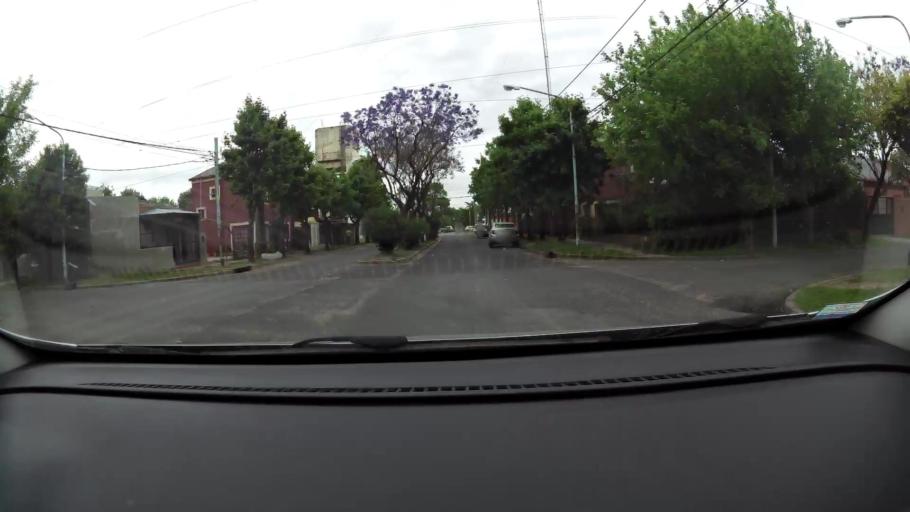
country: AR
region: Buenos Aires
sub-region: Partido de Campana
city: Campana
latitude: -34.1954
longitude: -58.9440
